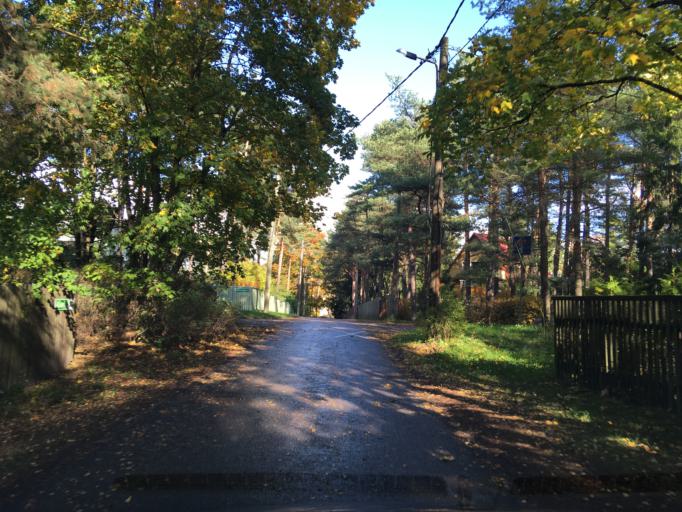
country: EE
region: Harju
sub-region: Tallinna linn
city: Tallinn
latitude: 59.3898
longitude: 24.7178
